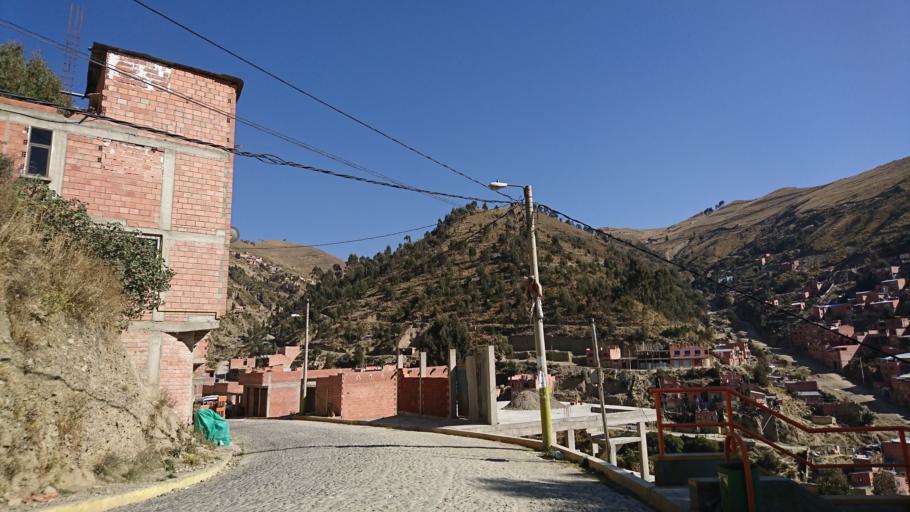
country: BO
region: La Paz
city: La Paz
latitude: -16.4693
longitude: -68.1243
